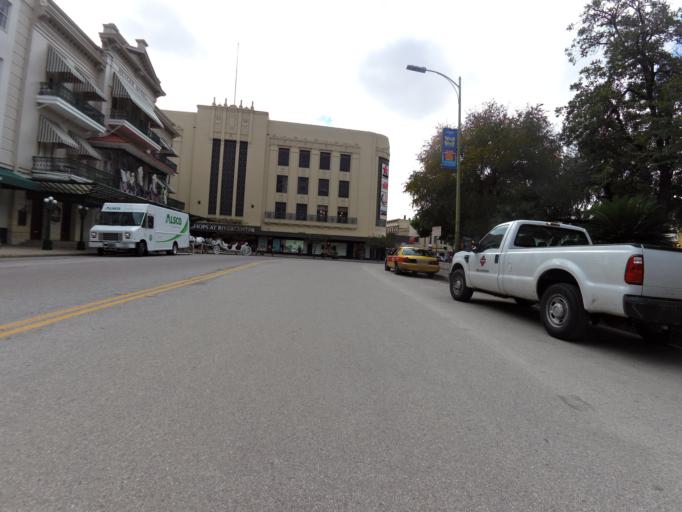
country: US
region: Texas
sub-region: Bexar County
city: San Antonio
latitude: 29.4250
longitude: -98.4866
